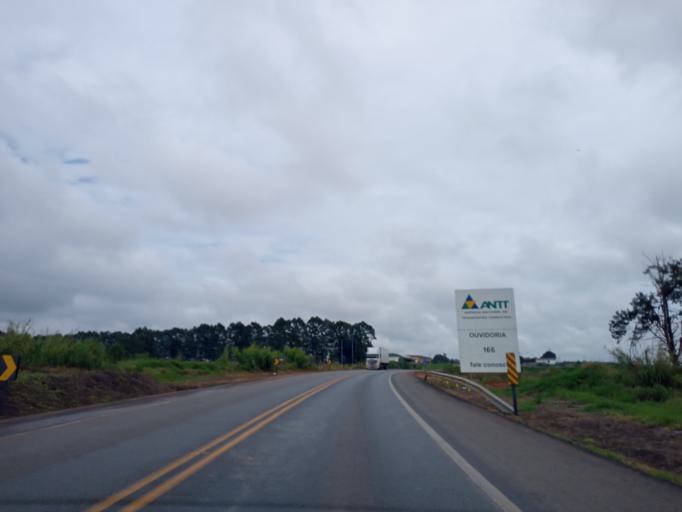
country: BR
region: Minas Gerais
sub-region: Campos Altos
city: Campos Altos
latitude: -19.6604
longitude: -46.2057
